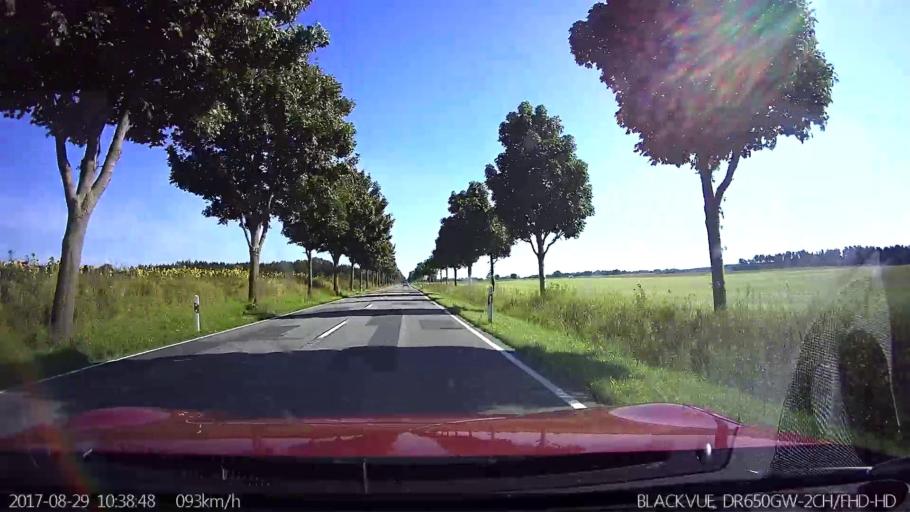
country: DE
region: Mecklenburg-Vorpommern
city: Franzburg
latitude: 54.1692
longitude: 12.8223
